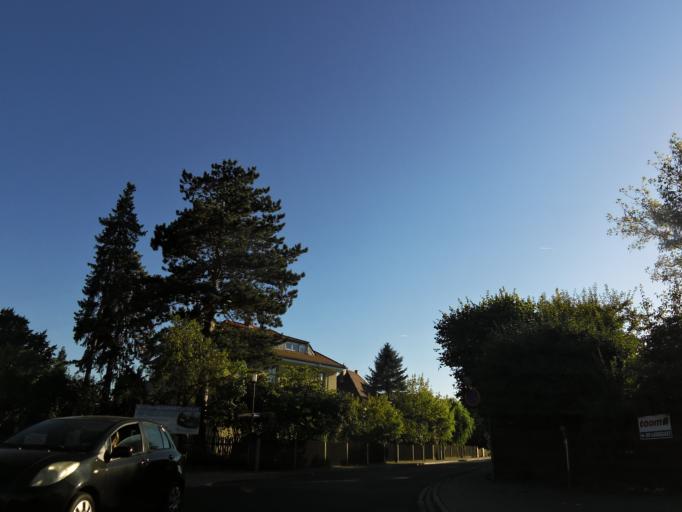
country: DE
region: Saxony
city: Dresden
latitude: 51.0076
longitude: 13.7679
